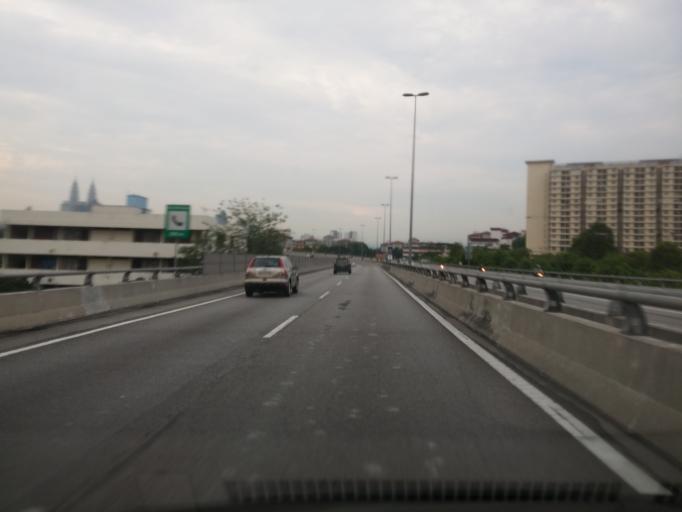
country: MY
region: Kuala Lumpur
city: Kuala Lumpur
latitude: 3.1257
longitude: 101.7185
